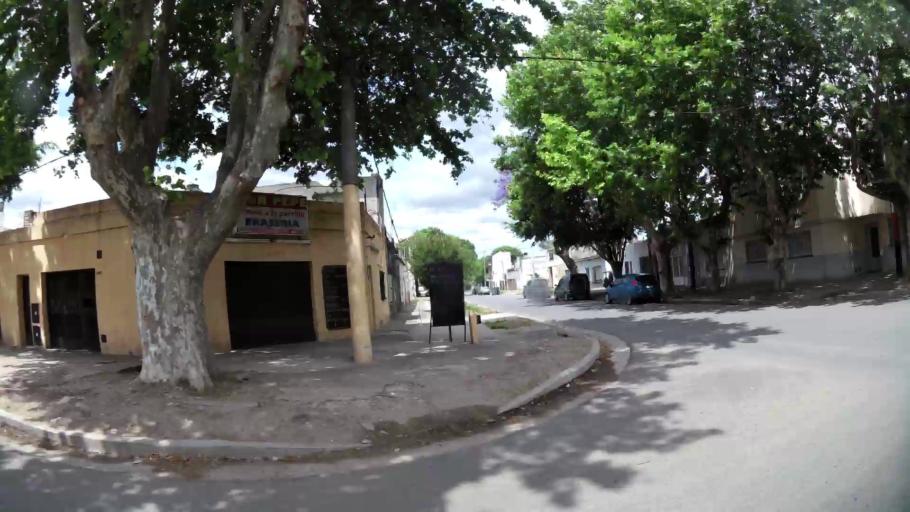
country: AR
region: Santa Fe
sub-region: Departamento de Rosario
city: Rosario
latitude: -32.9796
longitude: -60.6566
